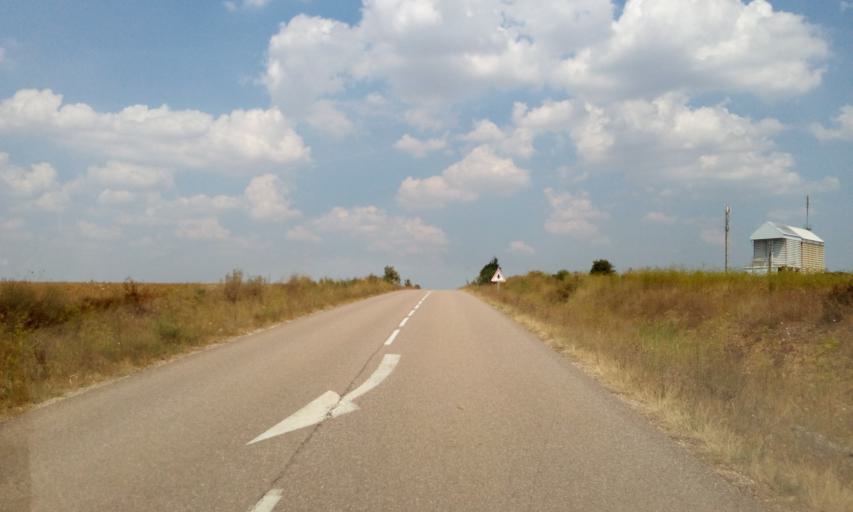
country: FR
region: Lorraine
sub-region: Departement de la Meuse
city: Vigneulles-les-Hattonchatel
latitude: 48.9616
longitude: 5.8583
